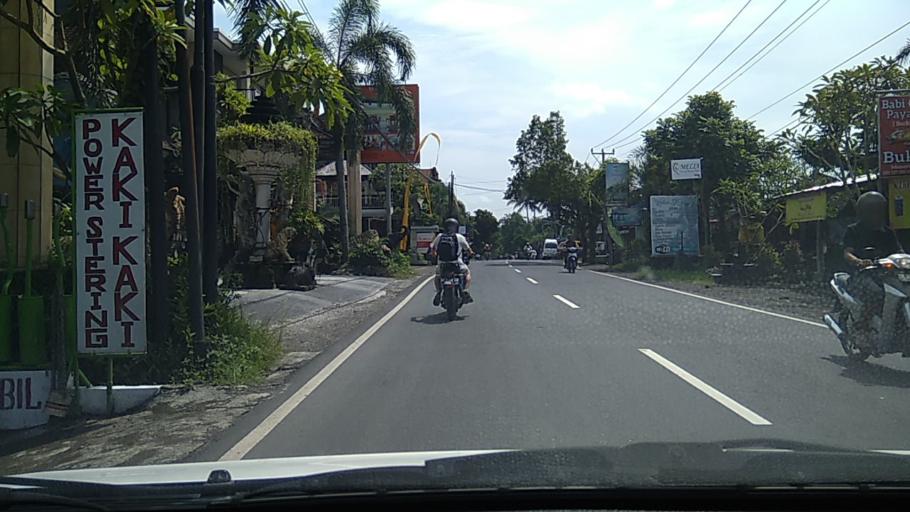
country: ID
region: Bali
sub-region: Kabupaten Gianyar
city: Ubud
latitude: -8.5230
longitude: 115.2777
